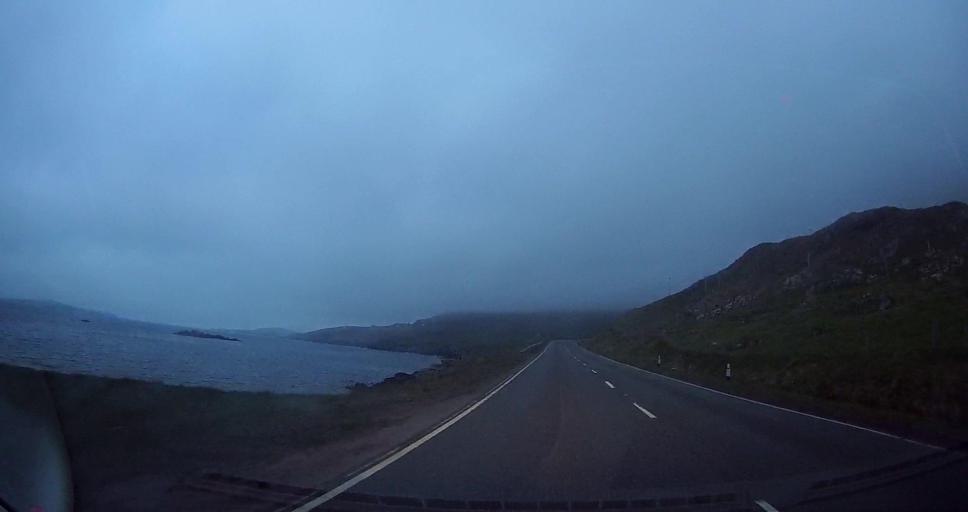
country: GB
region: Scotland
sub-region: Shetland Islands
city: Sandwick
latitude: 60.0342
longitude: -1.2331
